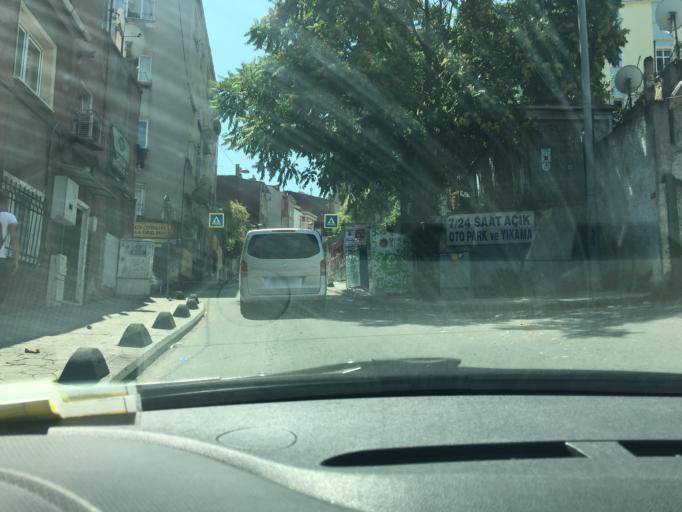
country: TR
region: Istanbul
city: Eminoenue
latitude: 41.0383
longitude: 28.9744
